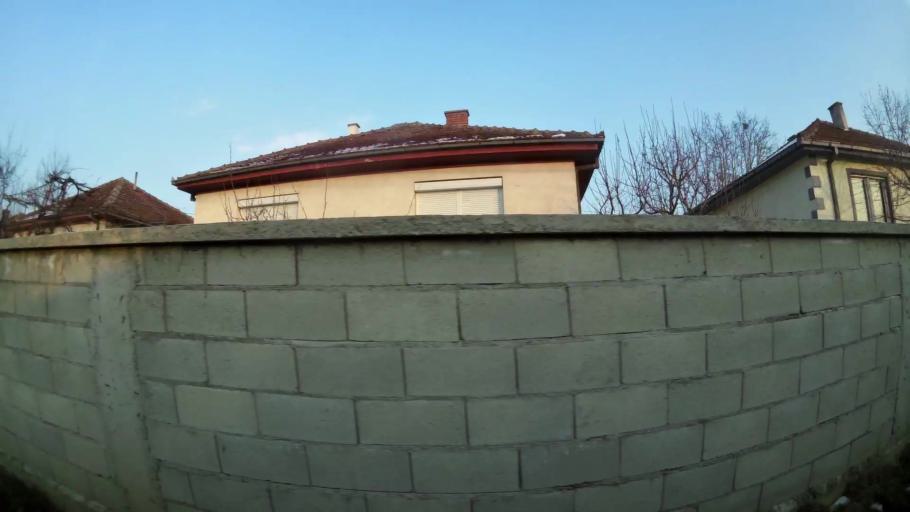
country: MK
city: Creshevo
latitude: 42.0148
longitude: 21.5207
